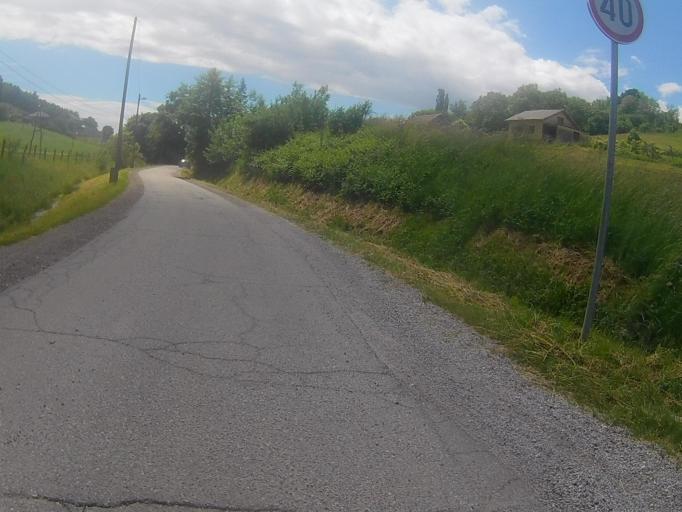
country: SI
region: Duplek
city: Zgornji Duplek
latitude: 46.5394
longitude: 15.7328
